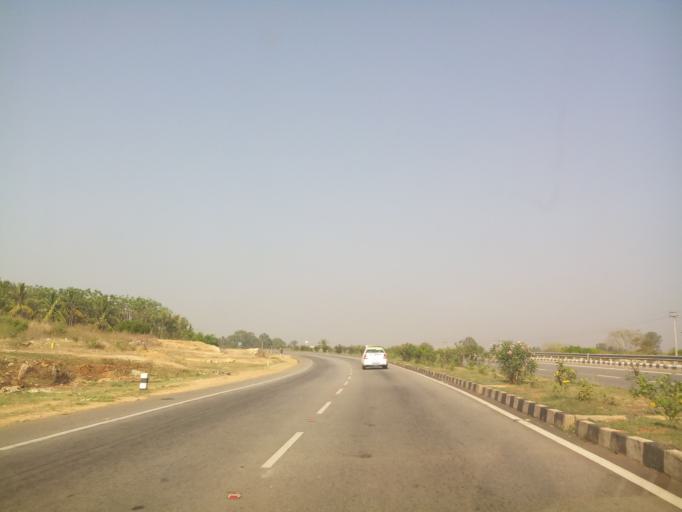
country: IN
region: Karnataka
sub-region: Bangalore Rural
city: Nelamangala
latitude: 13.0660
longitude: 77.3105
